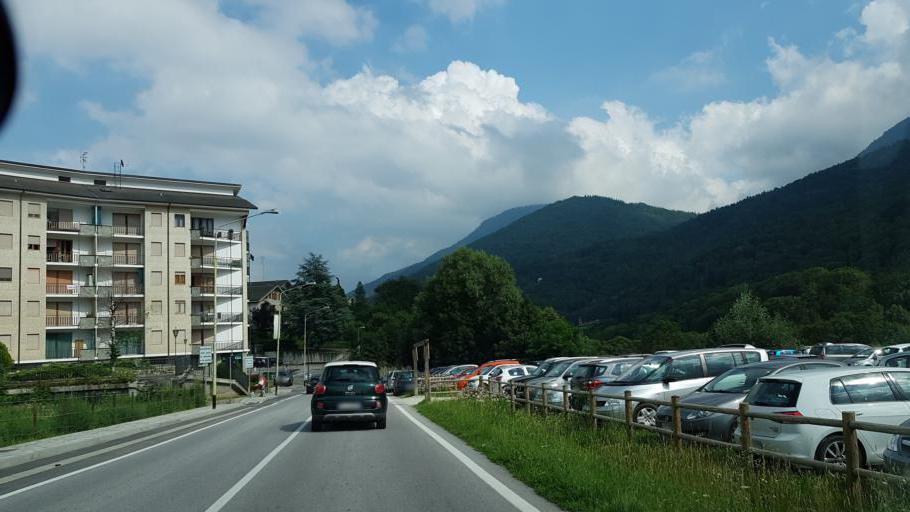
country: IT
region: Piedmont
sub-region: Provincia di Cuneo
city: Sampeyre
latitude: 44.5780
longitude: 7.1881
